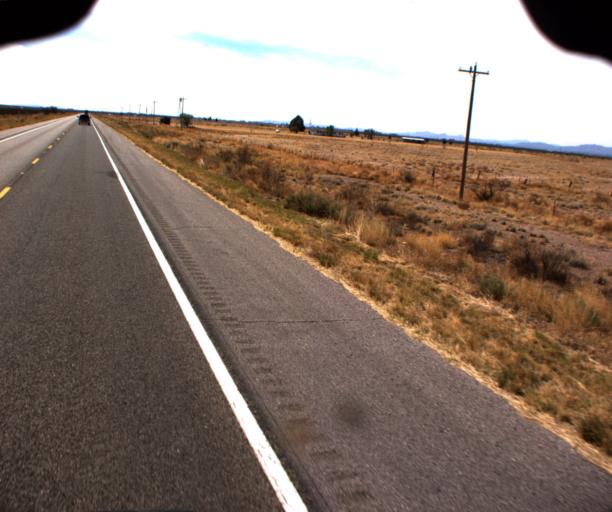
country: US
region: Arizona
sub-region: Cochise County
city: Pirtleville
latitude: 31.6642
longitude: -109.6797
